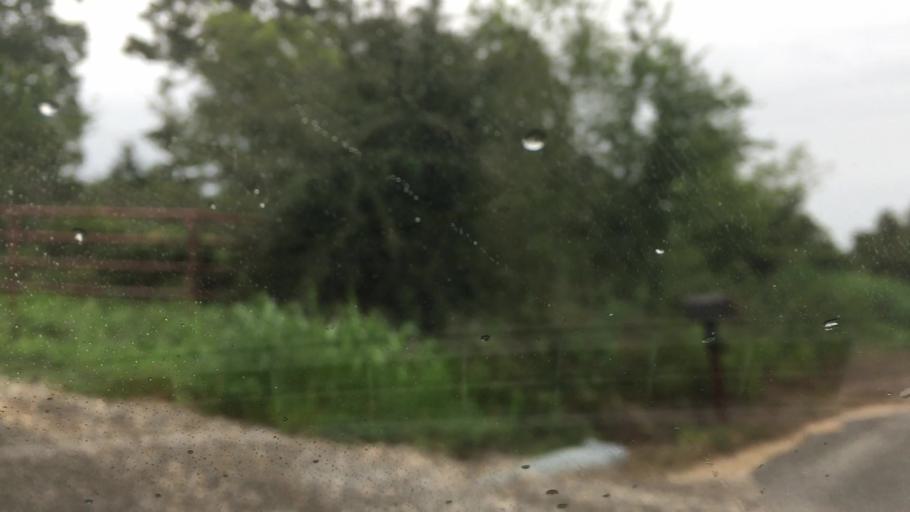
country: US
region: Oklahoma
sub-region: Muskogee County
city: Fort Gibson
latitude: 35.8973
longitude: -95.1627
